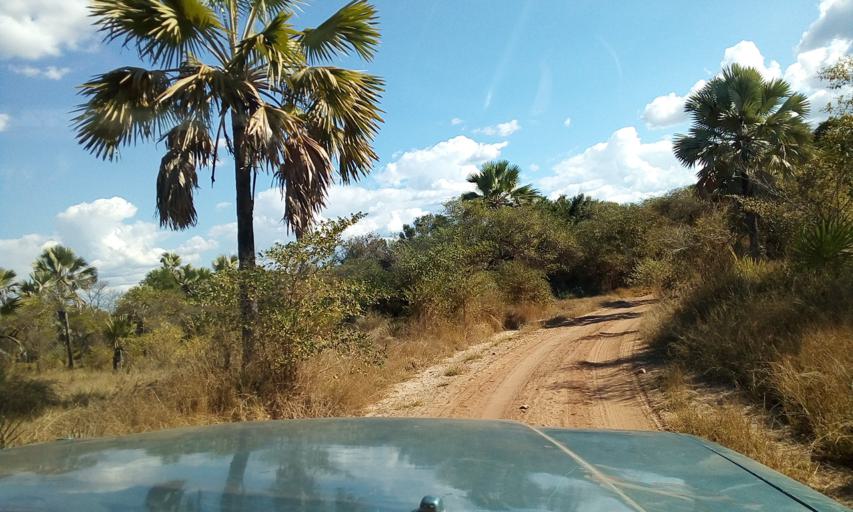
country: MG
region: Boeny
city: Mahajanga
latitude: -16.0621
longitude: 45.7943
